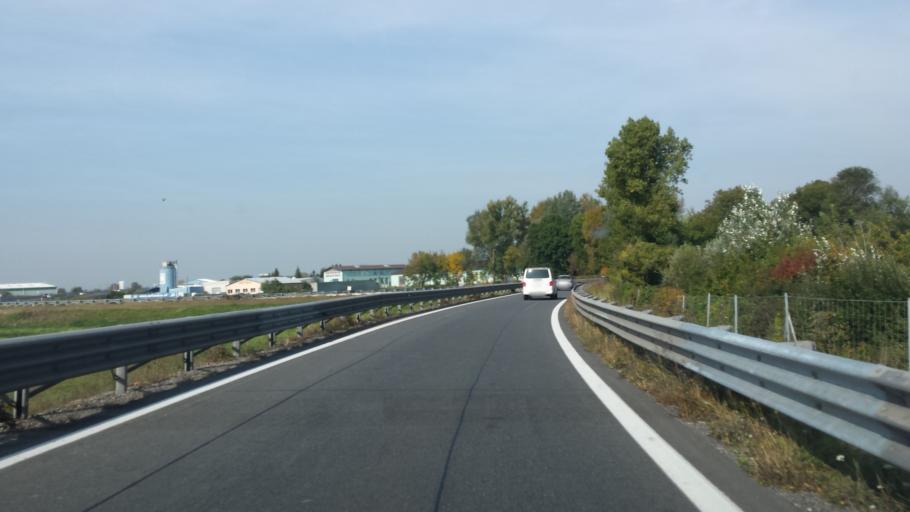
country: AT
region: Lower Austria
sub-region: Politischer Bezirk Korneuburg
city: Stockerau
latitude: 48.3823
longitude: 16.1893
